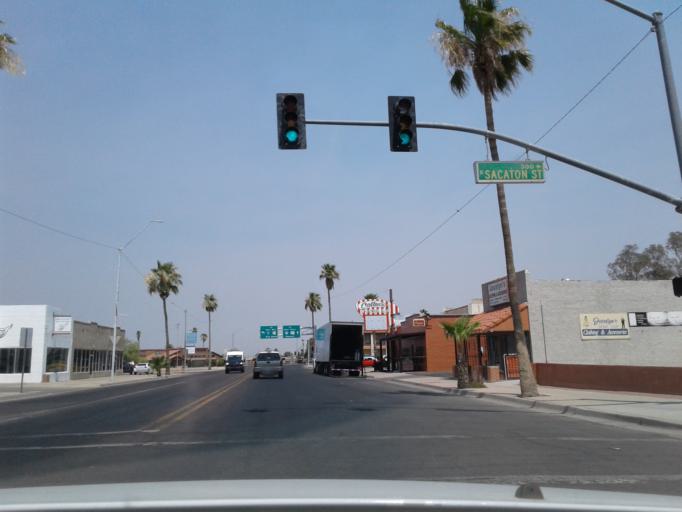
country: US
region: Arizona
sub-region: Pinal County
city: Casa Grande
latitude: 32.8781
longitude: -111.7553
